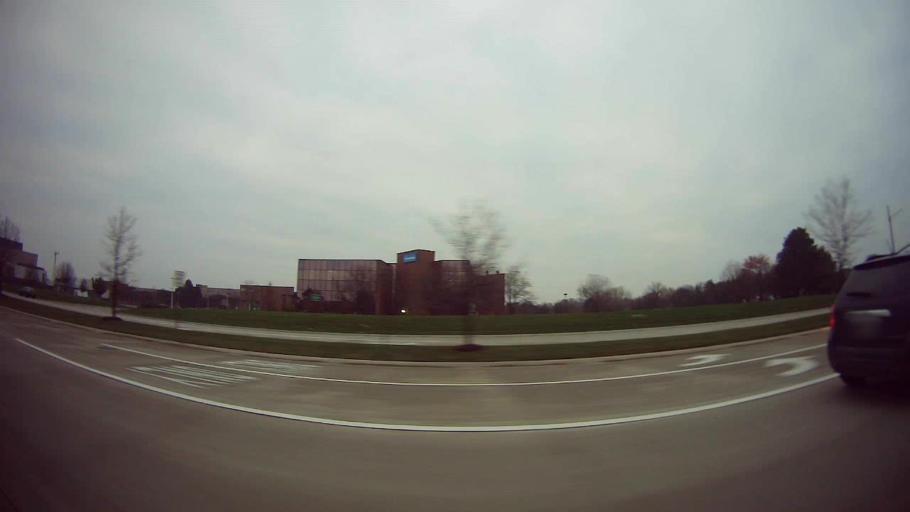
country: US
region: Michigan
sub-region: Oakland County
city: Birmingham
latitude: 42.5612
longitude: -83.1934
